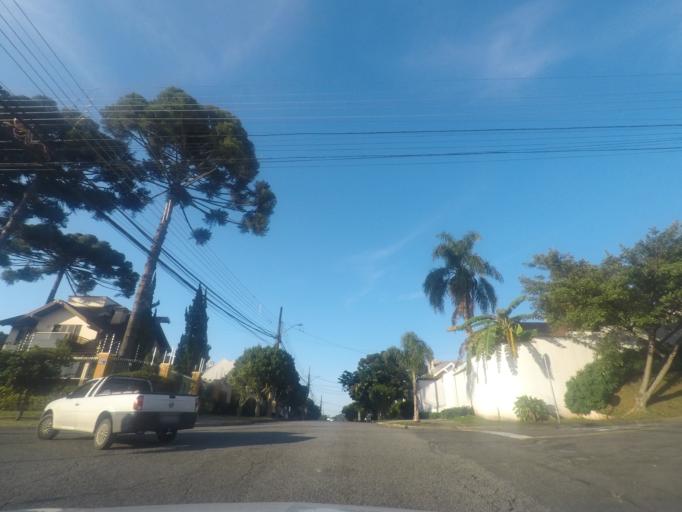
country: BR
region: Parana
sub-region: Curitiba
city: Curitiba
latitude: -25.4057
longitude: -49.2726
